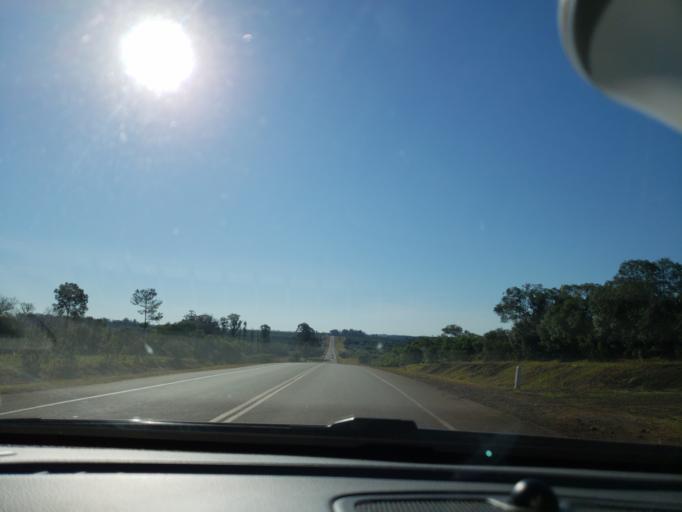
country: AR
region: Misiones
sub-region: Departamento de Apostoles
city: Apostoles
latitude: -27.8514
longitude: -55.7633
